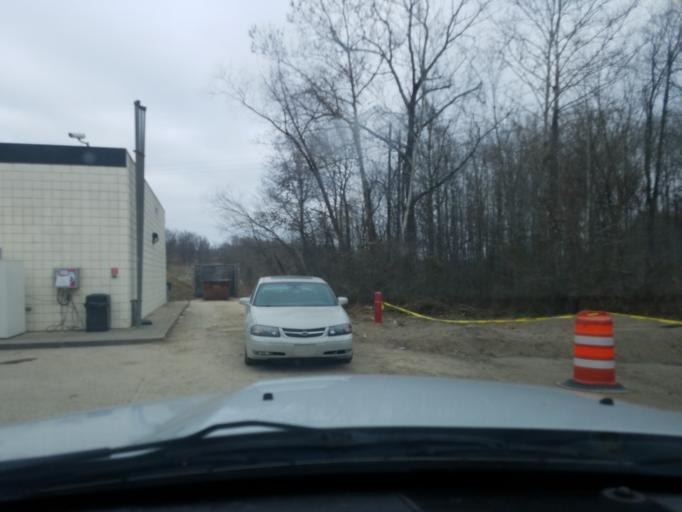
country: US
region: Indiana
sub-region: Daviess County
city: Odon
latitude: 38.9155
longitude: -86.9186
